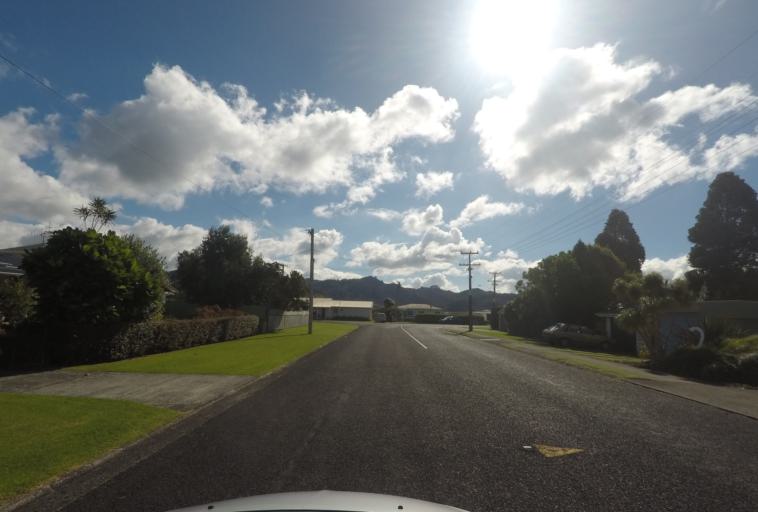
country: NZ
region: Bay of Plenty
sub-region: Western Bay of Plenty District
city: Waihi Beach
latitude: -37.4131
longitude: 175.9385
